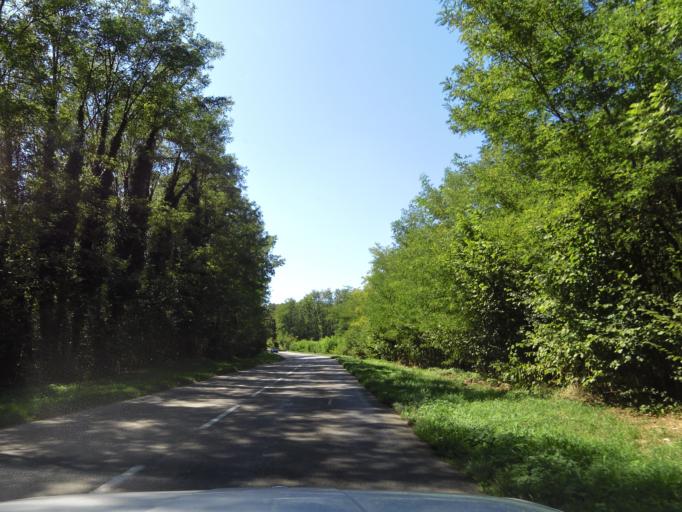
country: FR
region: Rhone-Alpes
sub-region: Departement de l'Ain
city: Leyment
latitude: 45.9213
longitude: 5.3176
